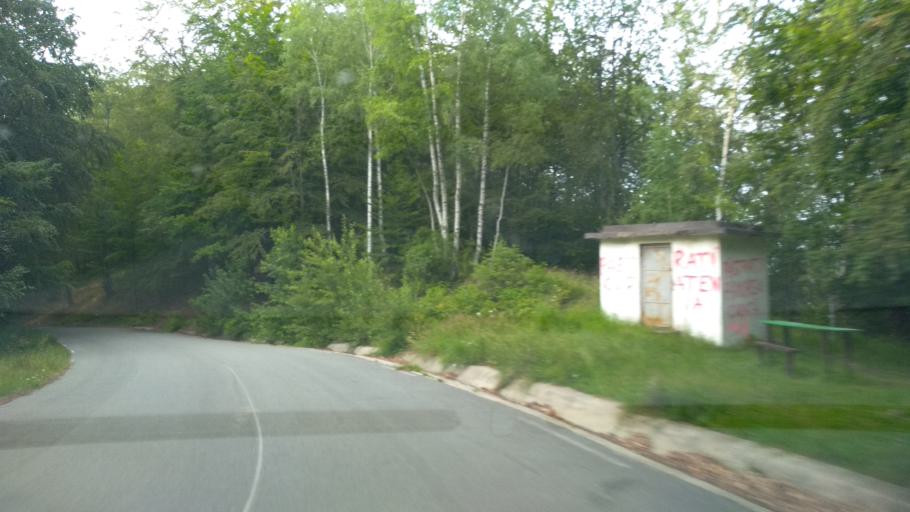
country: RO
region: Hunedoara
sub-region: Municipiul  Vulcan
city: Jiu-Paroseni
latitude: 45.3408
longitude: 23.2921
